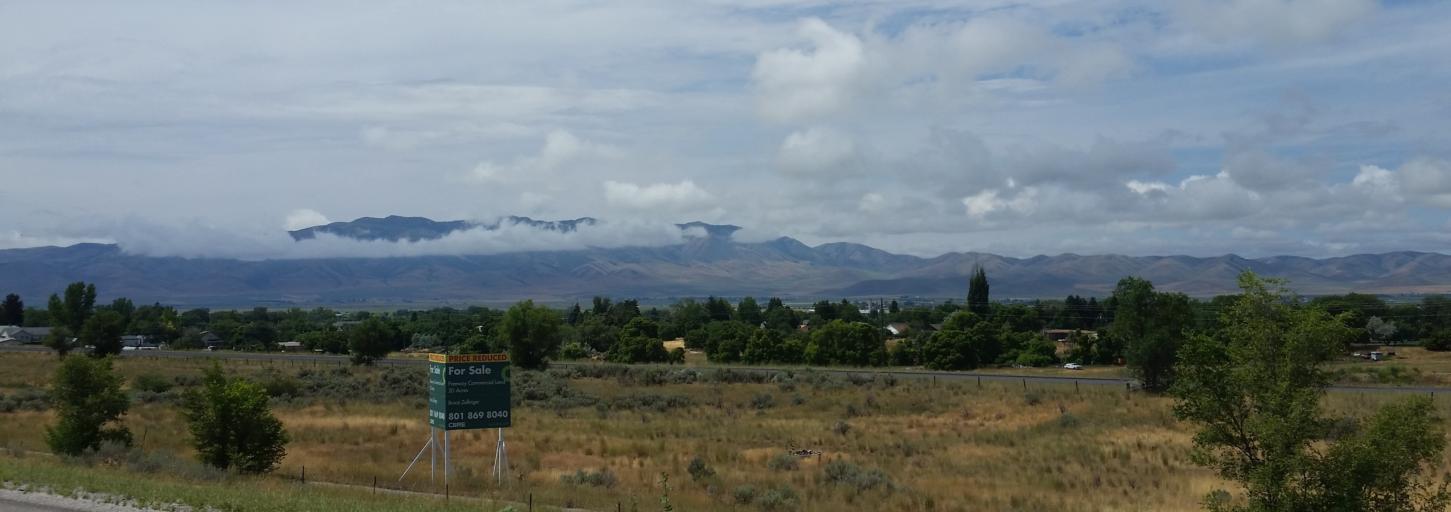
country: US
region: Idaho
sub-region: Oneida County
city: Malad City
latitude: 42.1939
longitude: -112.2371
